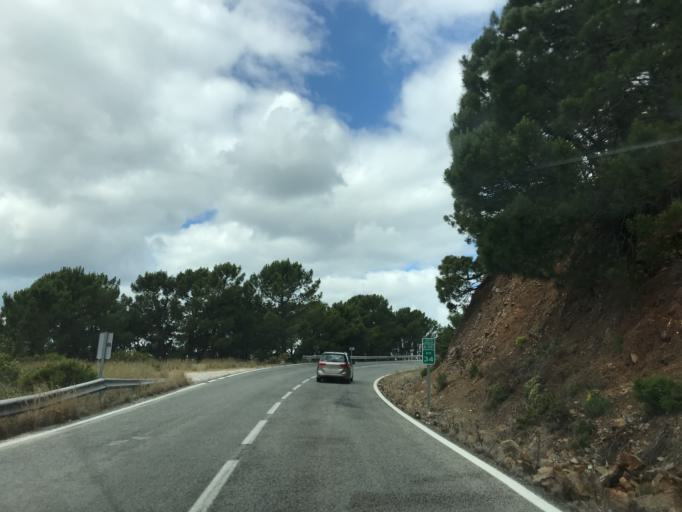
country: ES
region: Andalusia
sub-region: Provincia de Malaga
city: Benahavis
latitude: 36.5598
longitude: -5.0568
